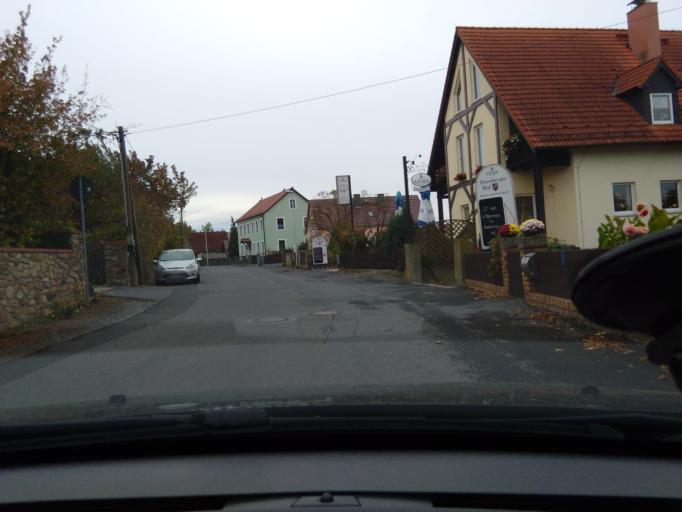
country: DE
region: Saxony
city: Moritzburg
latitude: 51.1600
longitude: 13.6766
